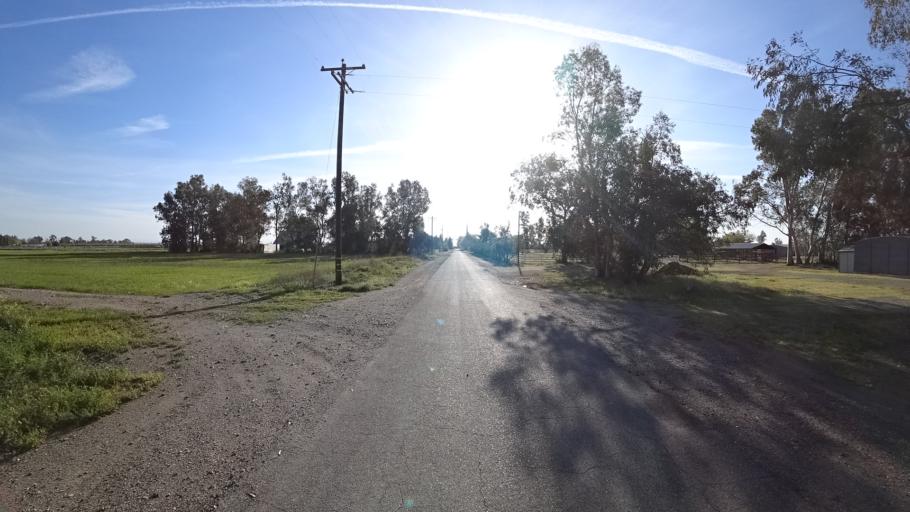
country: US
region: California
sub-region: Glenn County
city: Orland
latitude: 39.7331
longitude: -122.2130
